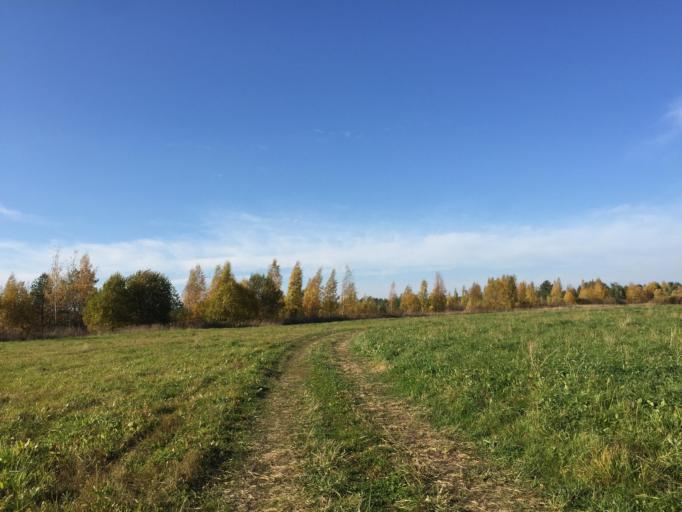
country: RU
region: Leningrad
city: Siverskiy
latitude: 59.3183
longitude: 30.0329
